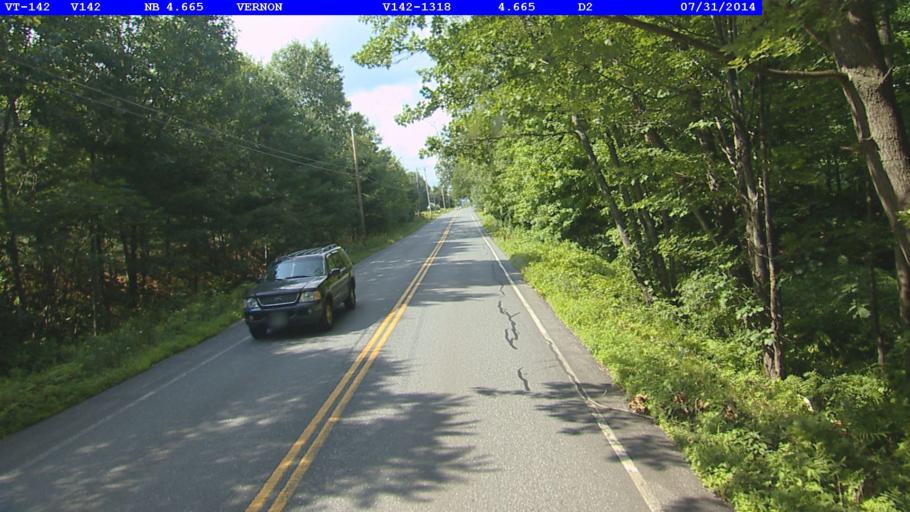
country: US
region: New Hampshire
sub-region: Cheshire County
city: Hinsdale
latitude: 42.7720
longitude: -72.5203
